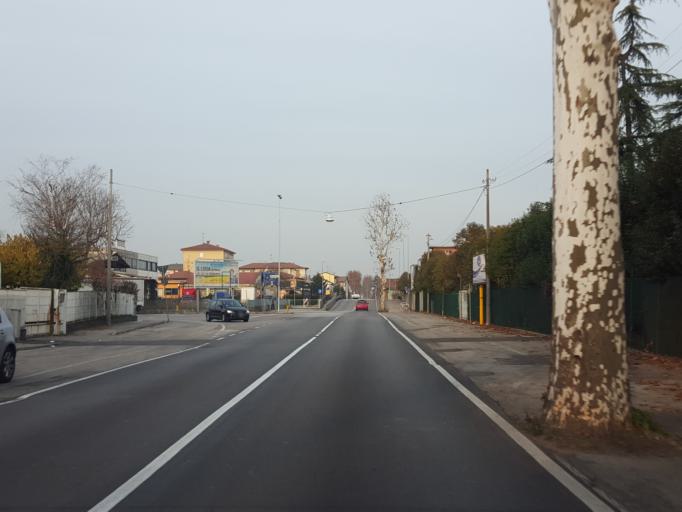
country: IT
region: Veneto
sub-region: Provincia di Vicenza
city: Creazzo
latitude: 45.5212
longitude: 11.5139
